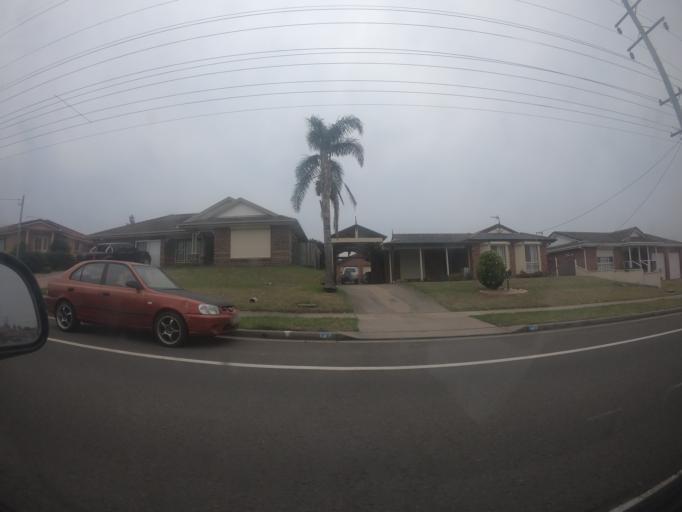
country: AU
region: New South Wales
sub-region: Shellharbour
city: Barrack Heights
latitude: -34.5745
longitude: 150.8393
